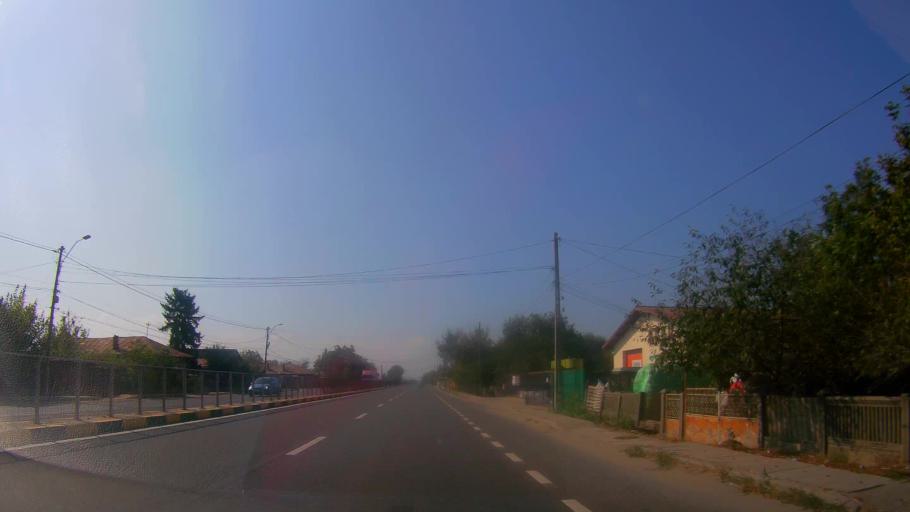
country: RO
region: Giurgiu
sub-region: Comuna Fratesti
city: Remus
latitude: 43.9473
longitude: 25.9800
